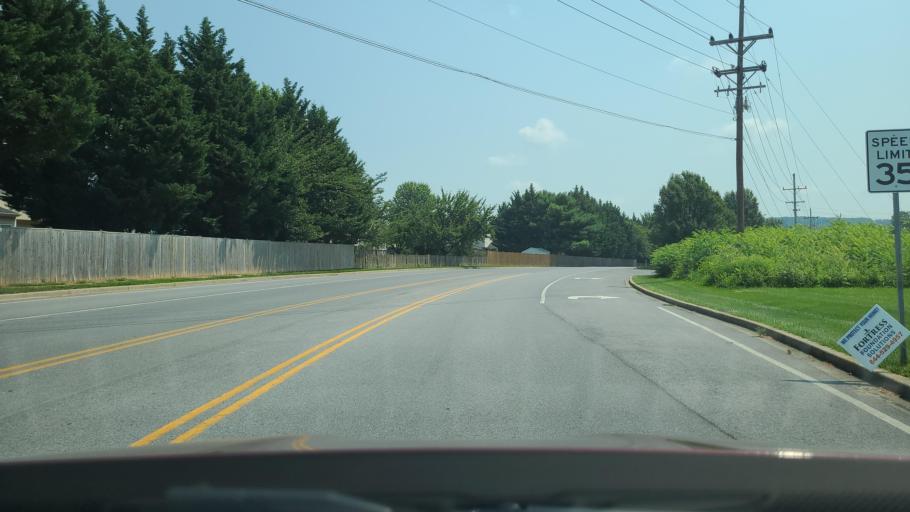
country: US
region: Maryland
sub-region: Frederick County
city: Jefferson
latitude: 39.3635
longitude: -77.5313
